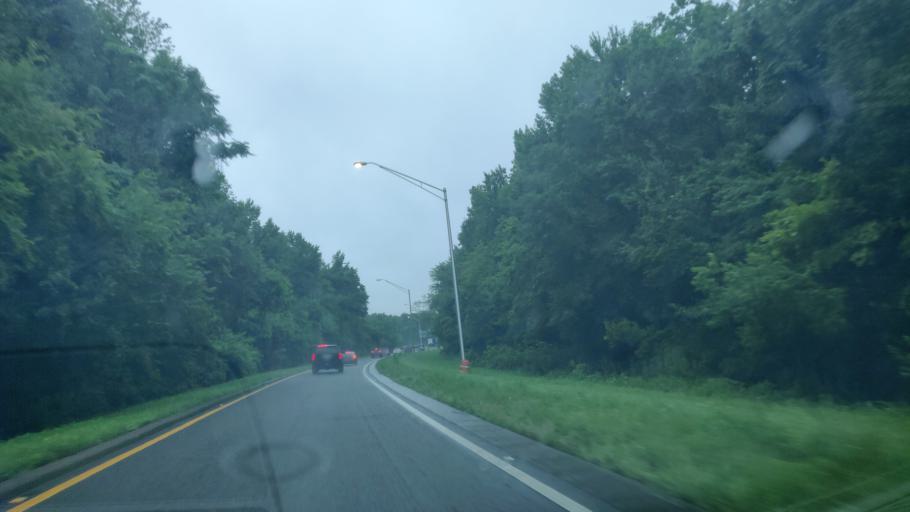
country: US
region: Florida
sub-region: Duval County
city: Jacksonville
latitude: 30.3129
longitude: -81.7719
